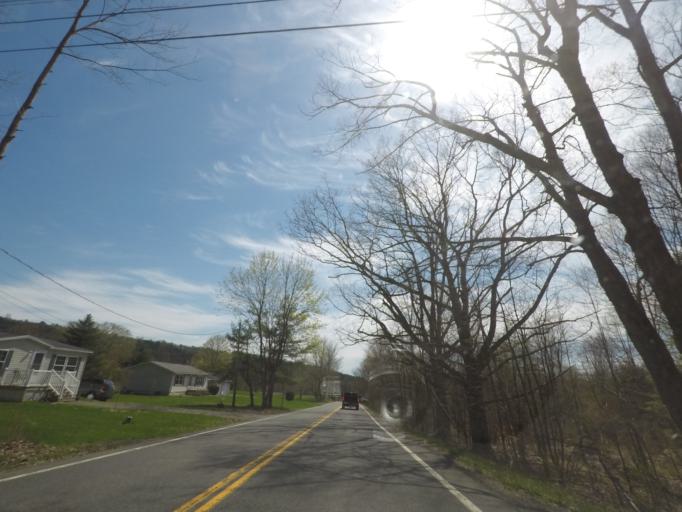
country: US
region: New York
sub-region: Columbia County
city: Chatham
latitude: 42.4221
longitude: -73.5068
